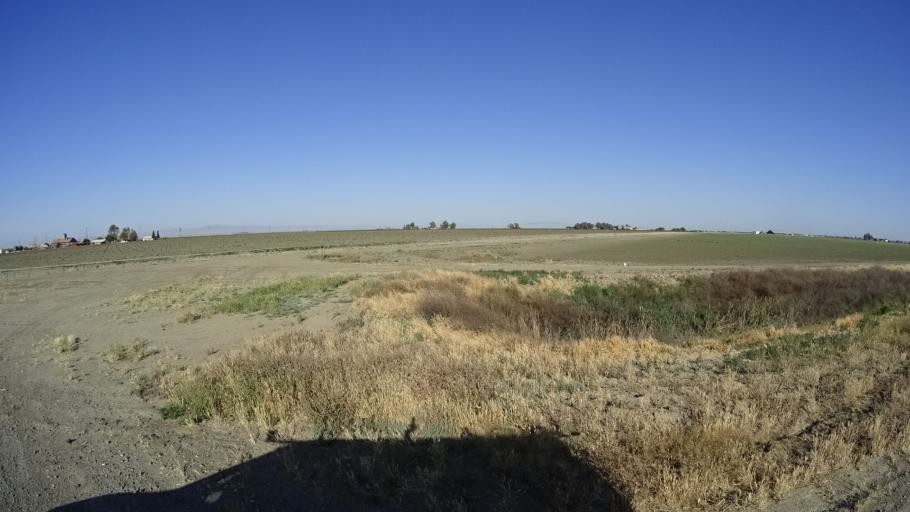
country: US
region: California
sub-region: Kings County
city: Stratford
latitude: 36.1546
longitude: -119.7980
